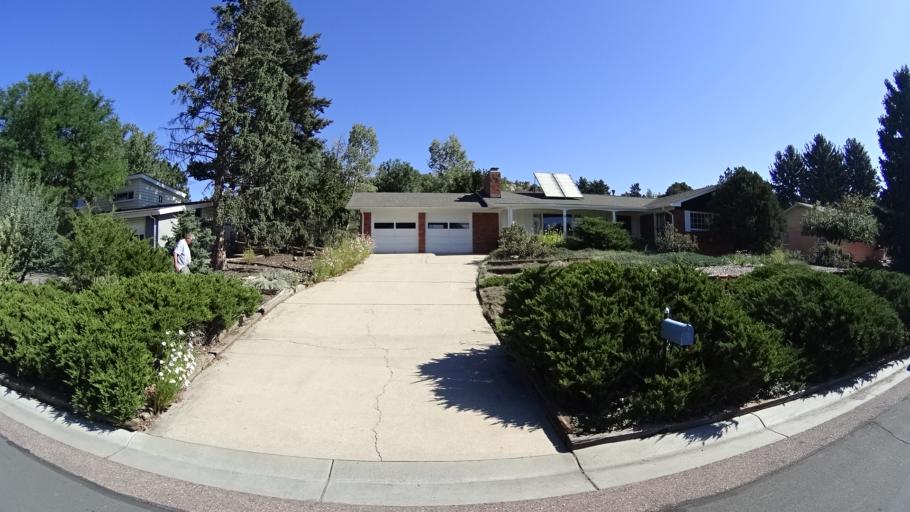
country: US
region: Colorado
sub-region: El Paso County
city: Colorado Springs
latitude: 38.8694
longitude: -104.7784
